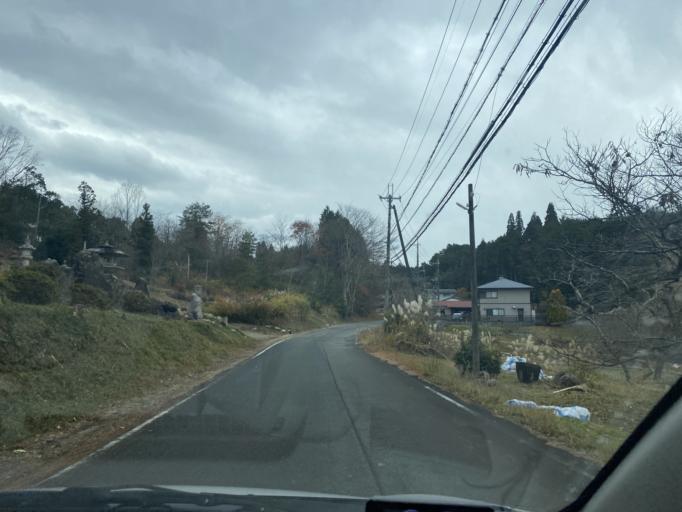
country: JP
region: Kyoto
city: Kameoka
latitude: 35.0553
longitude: 135.4527
